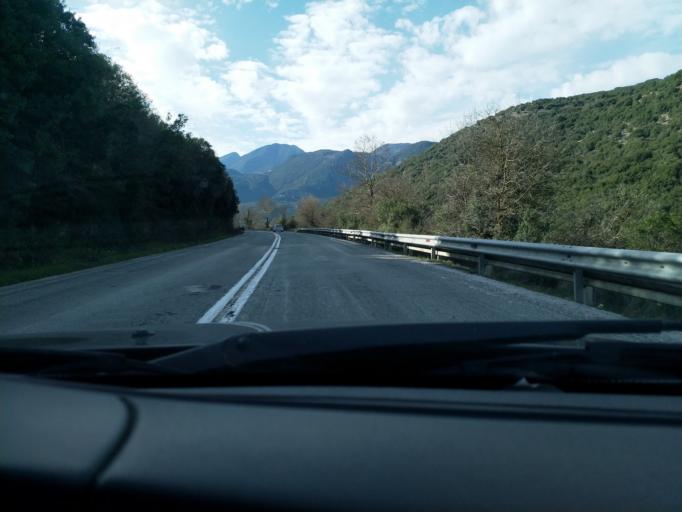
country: GR
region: Epirus
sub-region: Nomos Ioanninon
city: Agia Kyriaki
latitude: 39.4455
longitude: 20.8574
